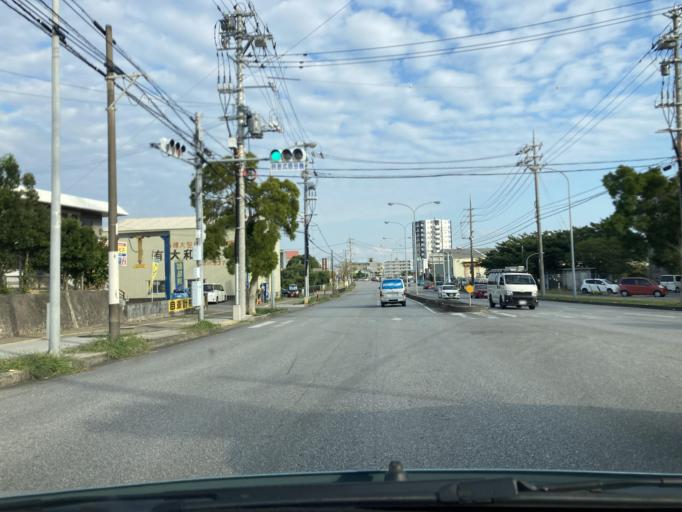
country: JP
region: Okinawa
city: Okinawa
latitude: 26.3540
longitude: 127.8068
